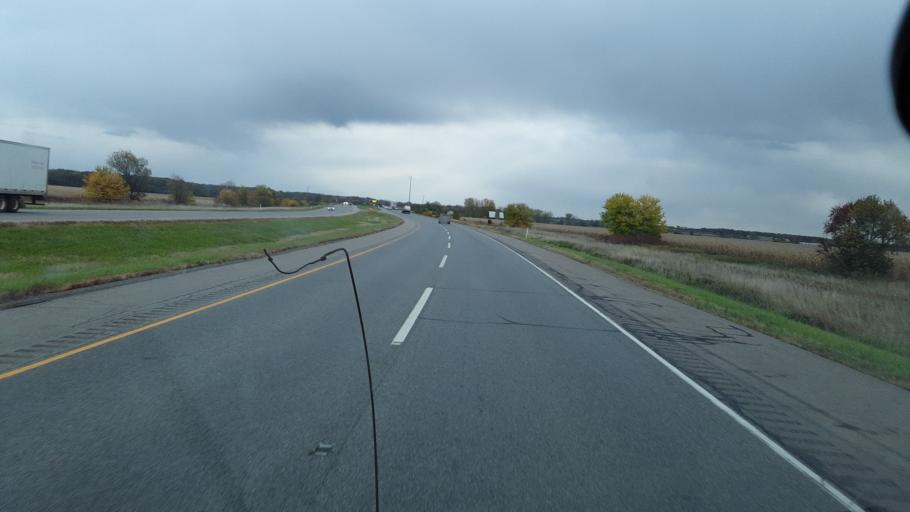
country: US
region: Indiana
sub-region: Saint Joseph County
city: New Carlisle
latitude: 41.7521
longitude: -86.4353
